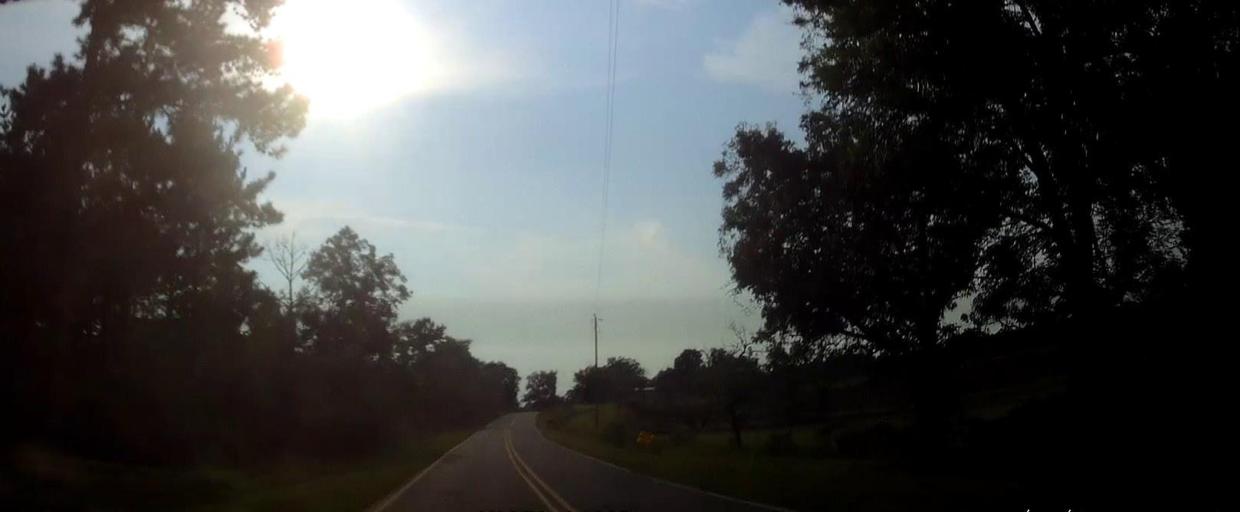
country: US
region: Georgia
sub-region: Laurens County
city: Dublin
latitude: 32.4808
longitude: -82.9626
